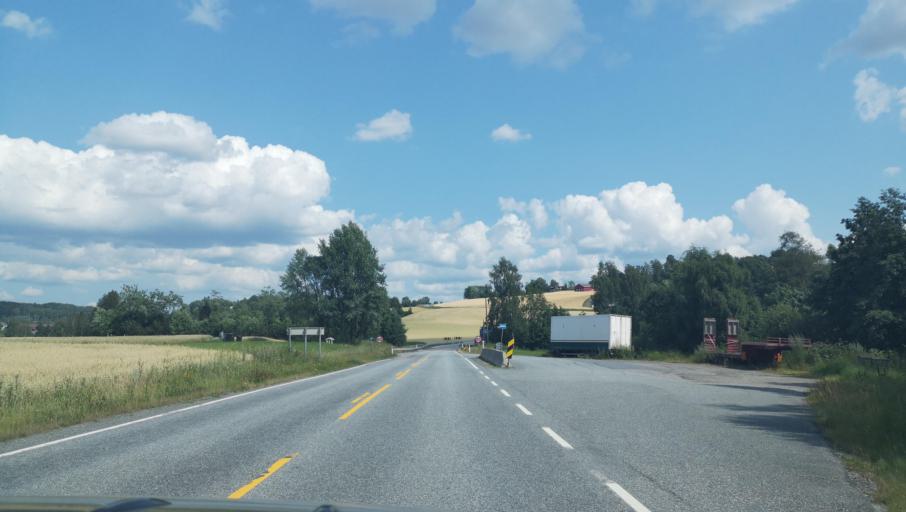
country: NO
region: Buskerud
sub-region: Ovre Eiker
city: Hokksund
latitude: 59.7247
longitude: 9.8328
